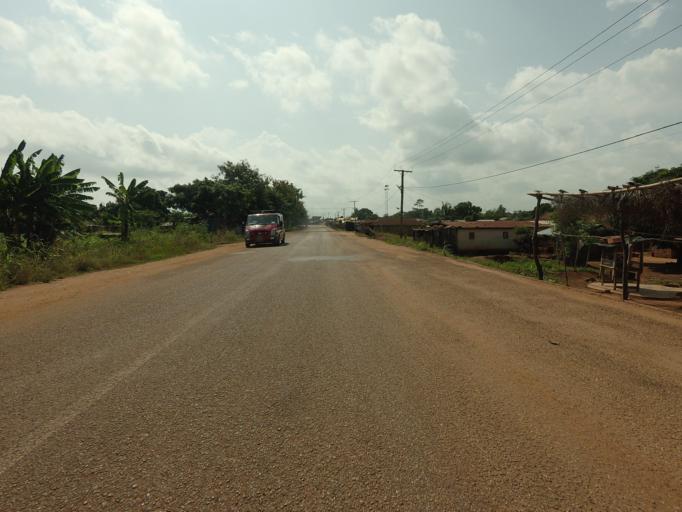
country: TG
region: Maritime
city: Tsevie
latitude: 6.3588
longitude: 0.8666
